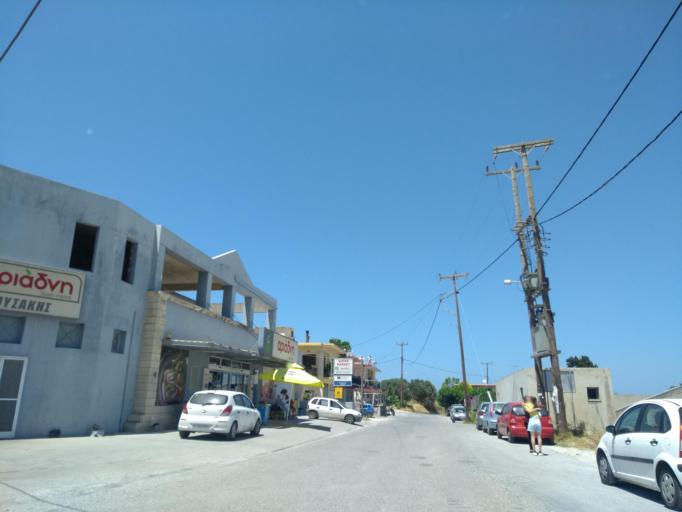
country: GR
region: Crete
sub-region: Nomos Chanias
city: Georgioupolis
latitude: 35.3321
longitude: 24.3354
